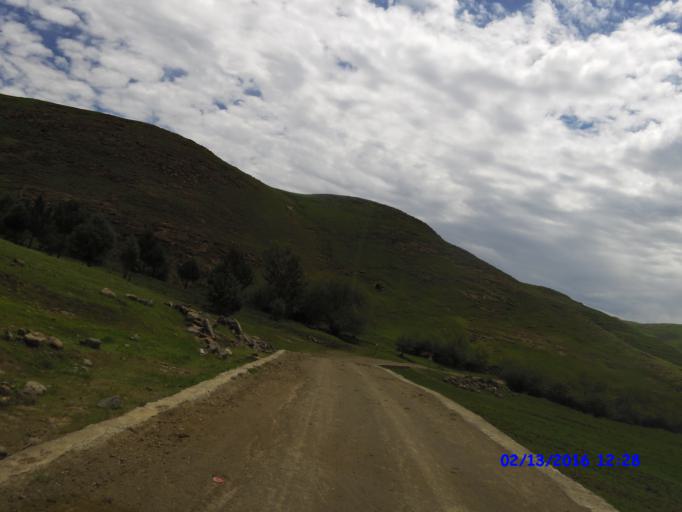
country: LS
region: Maseru
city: Nako
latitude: -29.8656
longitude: 28.0381
